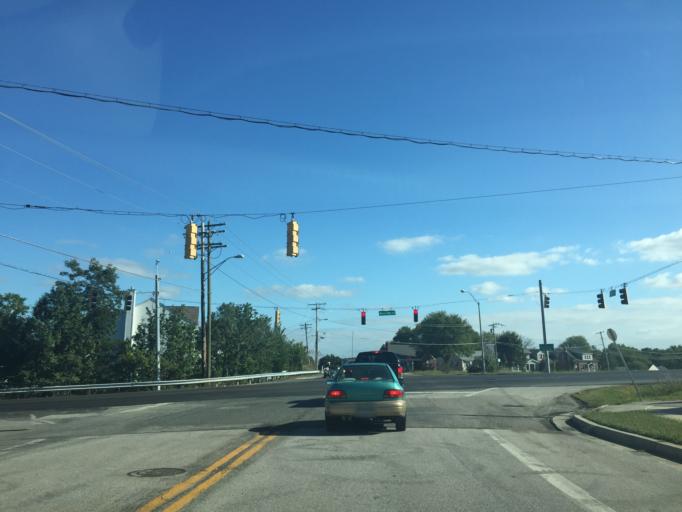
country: US
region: Maryland
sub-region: Baltimore County
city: Rossville
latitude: 39.3641
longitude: -76.4915
